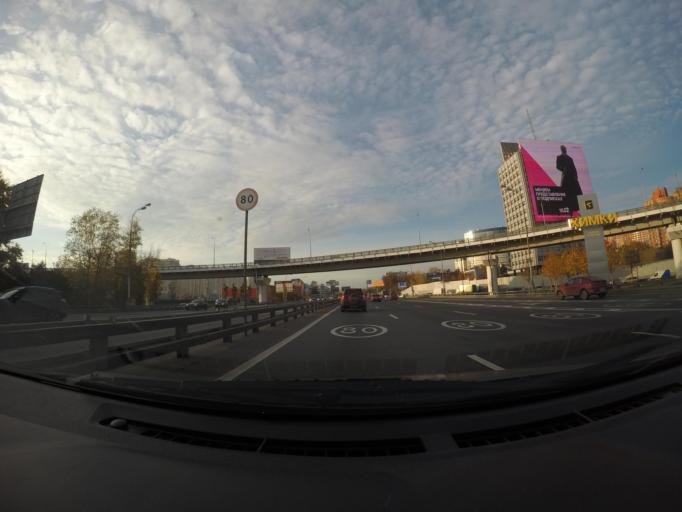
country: RU
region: Moscow
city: Khimki
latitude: 55.8822
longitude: 37.4444
